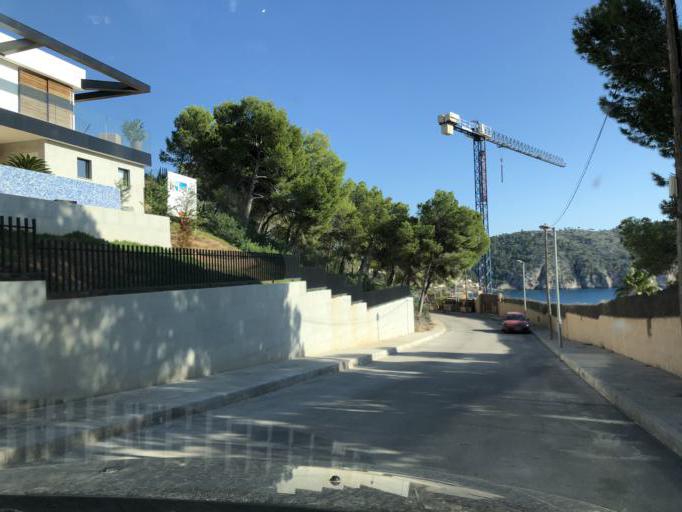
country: ES
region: Balearic Islands
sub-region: Illes Balears
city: Camp de Mar
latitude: 39.5400
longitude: 2.4112
